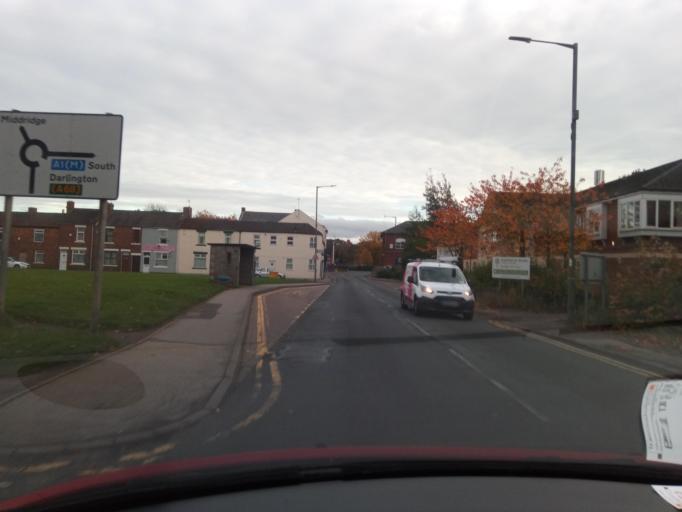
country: GB
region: England
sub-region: County Durham
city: Shildon
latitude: 54.6262
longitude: -1.6482
